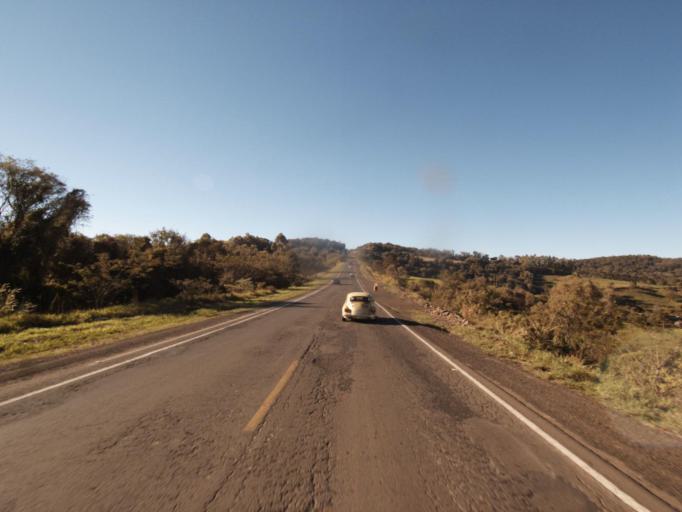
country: AR
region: Misiones
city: Bernardo de Irigoyen
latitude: -26.5800
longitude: -53.5158
